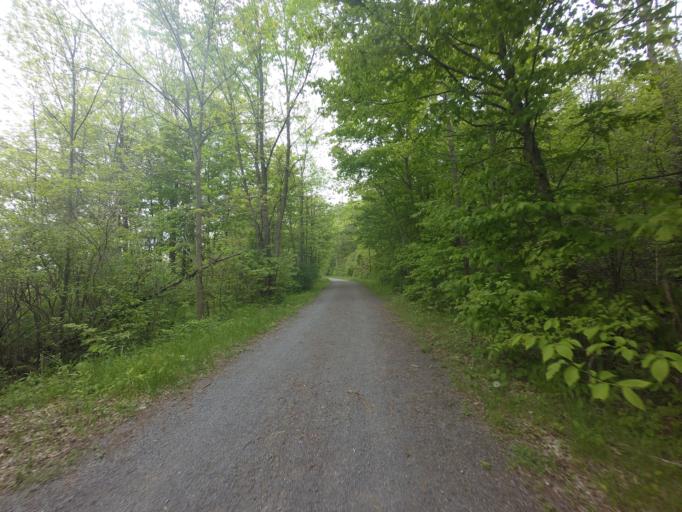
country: CA
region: Ontario
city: Kingston
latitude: 44.3040
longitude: -76.5627
